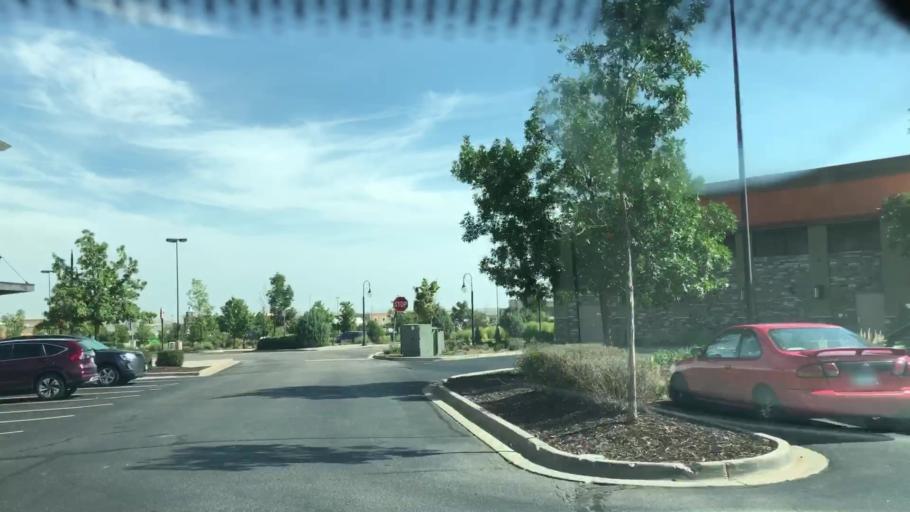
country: US
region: Colorado
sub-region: Douglas County
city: Parker
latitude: 39.6018
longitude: -104.7085
